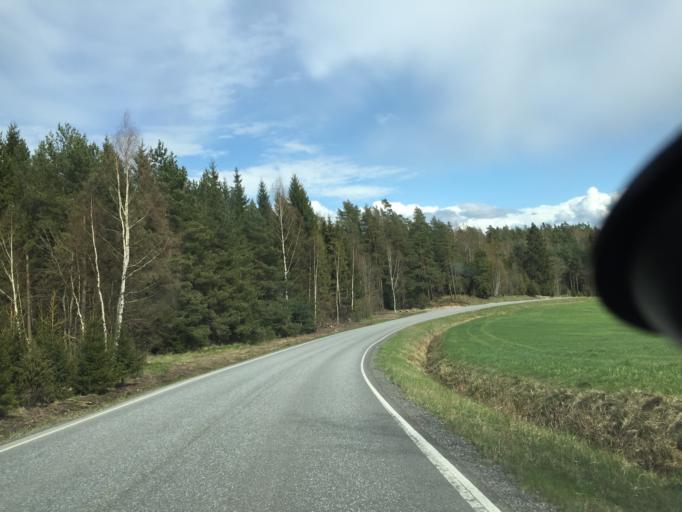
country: FI
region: Varsinais-Suomi
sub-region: Salo
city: Pernioe
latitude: 60.0334
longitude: 23.1880
